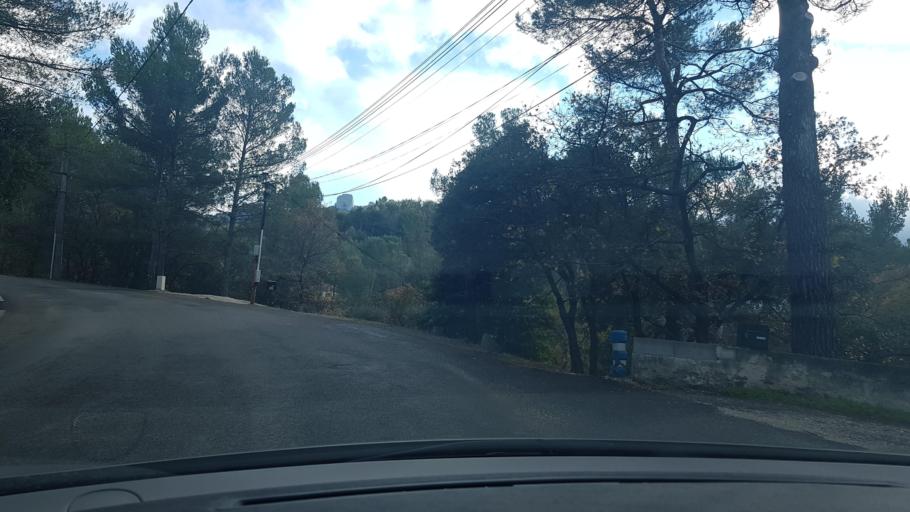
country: FR
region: Provence-Alpes-Cote d'Azur
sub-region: Departement des Bouches-du-Rhone
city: Simiane-Collongue
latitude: 43.4231
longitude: 5.4505
